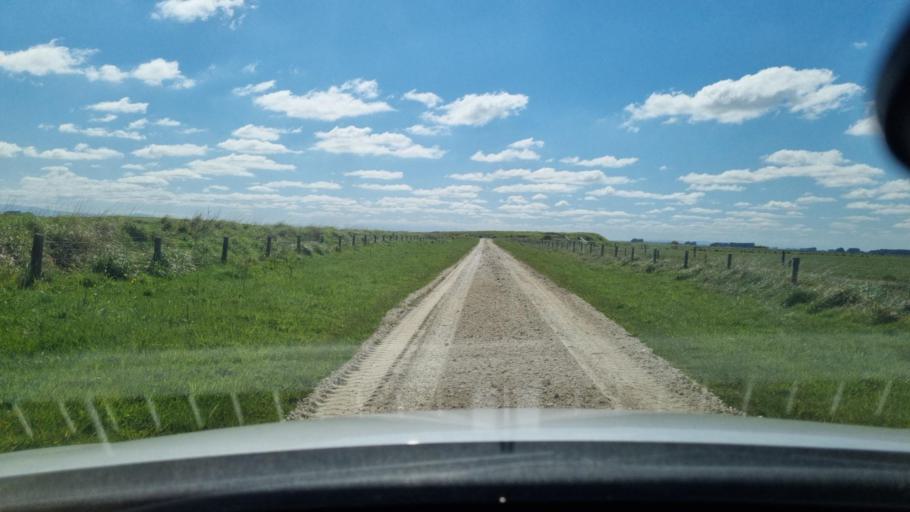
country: NZ
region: Southland
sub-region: Invercargill City
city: Invercargill
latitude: -46.3877
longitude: 168.2584
